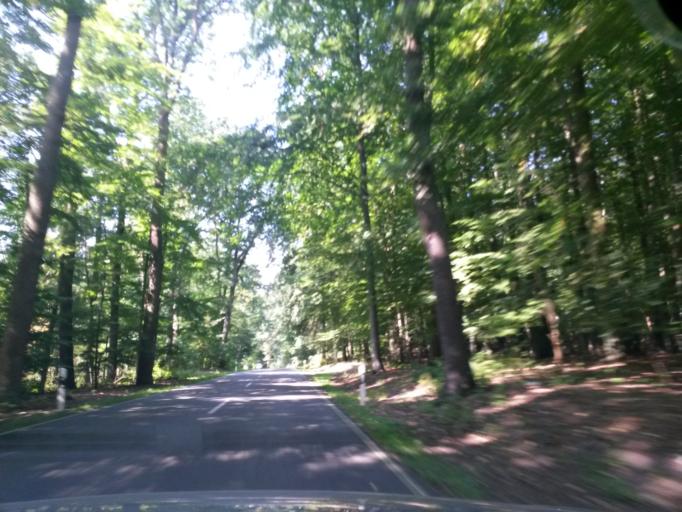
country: DE
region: Brandenburg
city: Marienwerder
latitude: 52.9110
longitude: 13.6530
